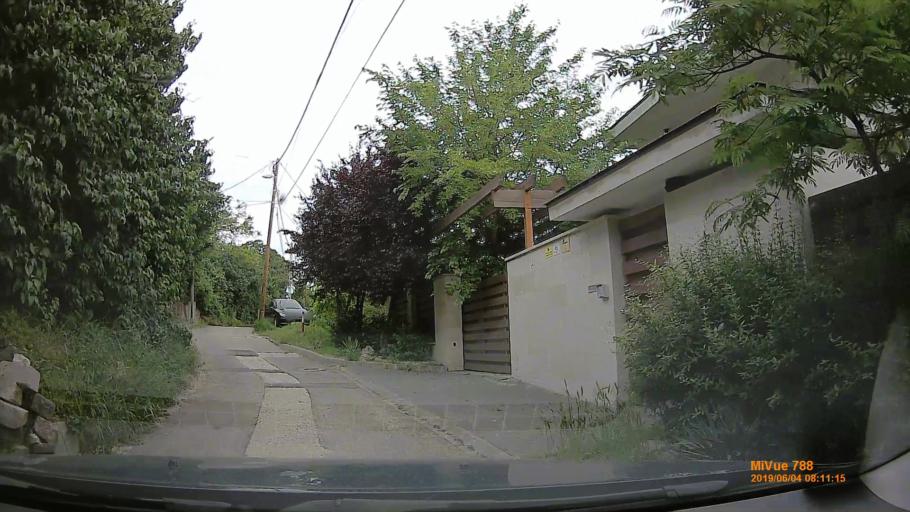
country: HU
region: Budapest
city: Budapest XXII. keruelet
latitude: 47.4401
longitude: 19.0159
